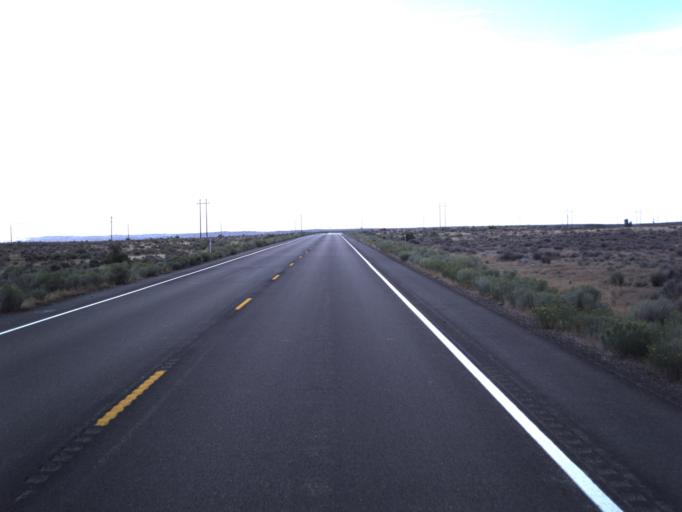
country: US
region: Utah
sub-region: Uintah County
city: Naples
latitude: 40.2247
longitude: -109.3956
